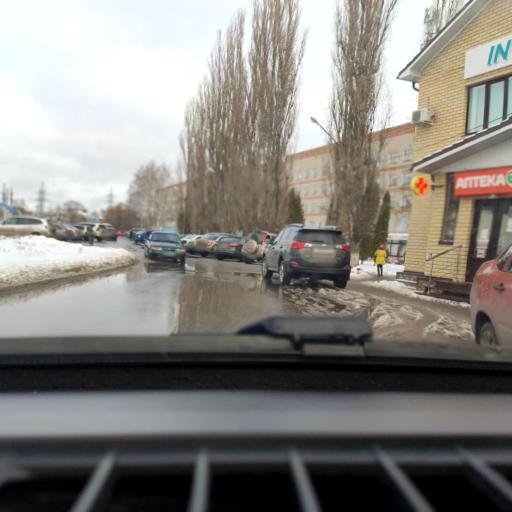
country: RU
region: Voronezj
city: Semiluki
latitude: 51.7004
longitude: 39.0224
